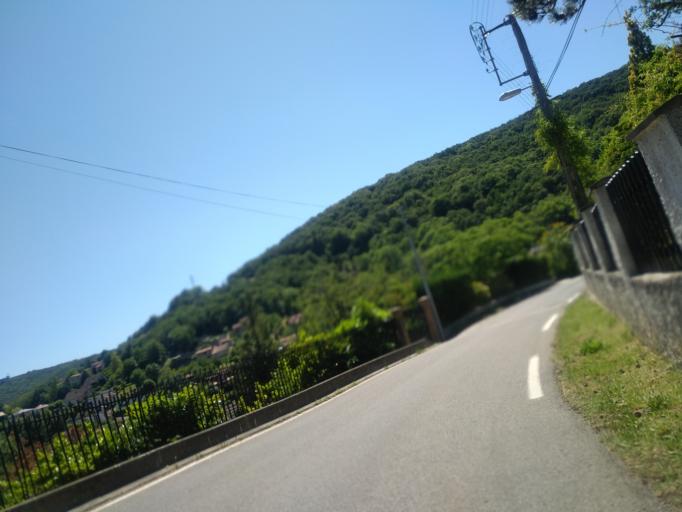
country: FR
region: Rhone-Alpes
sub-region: Departement du Rhone
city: Albigny-sur-Saone
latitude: 45.8464
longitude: 4.8210
